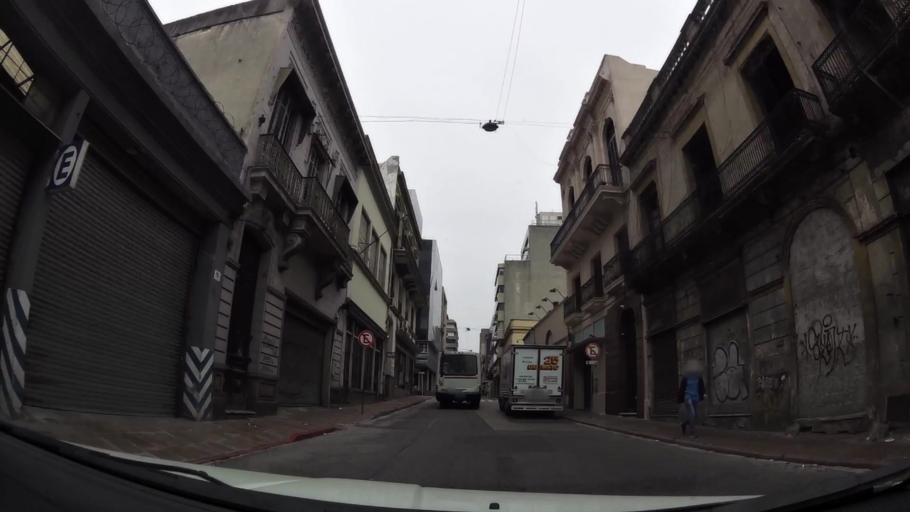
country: UY
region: Montevideo
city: Montevideo
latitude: -34.9047
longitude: -56.2023
